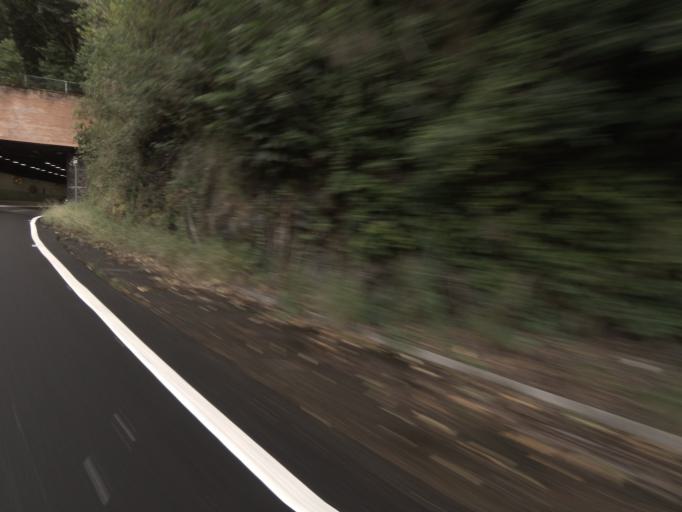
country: US
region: Hawaii
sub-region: Honolulu County
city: Kane'ohe
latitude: 21.3799
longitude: -157.8118
